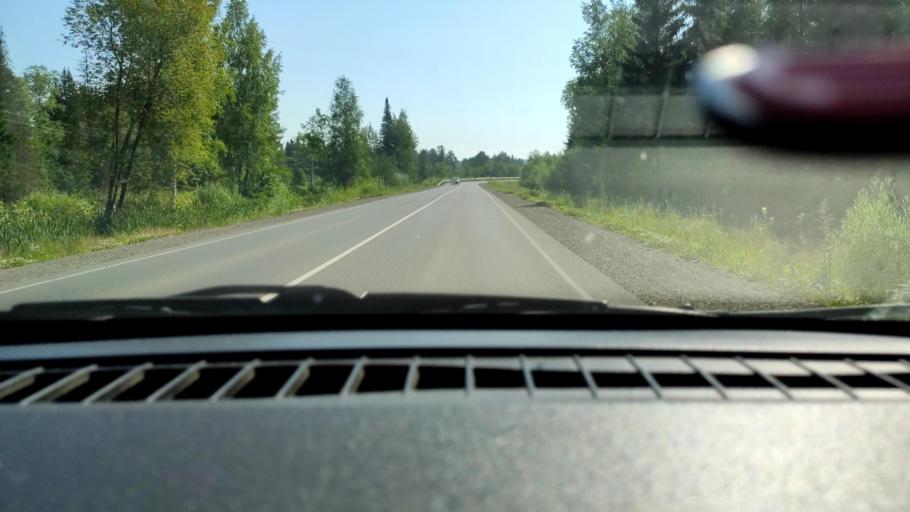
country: RU
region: Perm
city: Nytva
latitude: 57.9358
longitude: 55.5093
